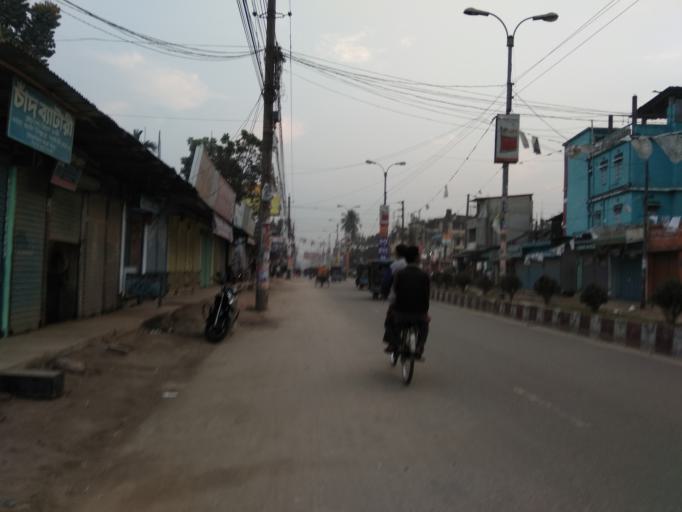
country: BD
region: Rangpur Division
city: Rangpur
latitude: 25.7372
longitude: 89.2548
